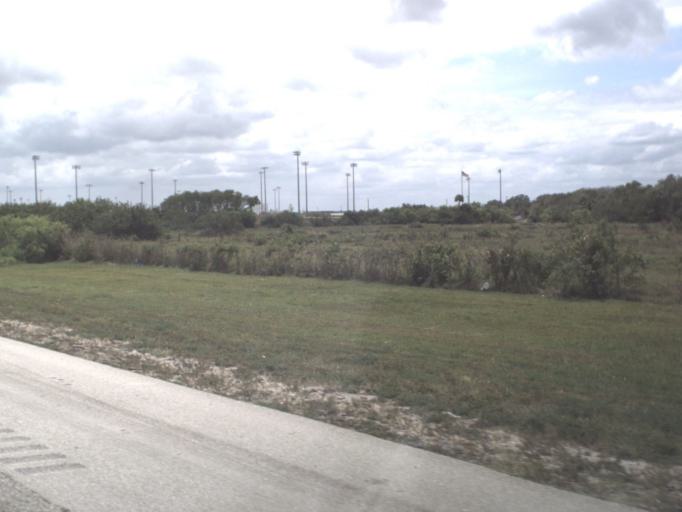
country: US
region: Florida
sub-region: Brevard County
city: Rockledge
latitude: 28.2590
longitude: -80.7270
